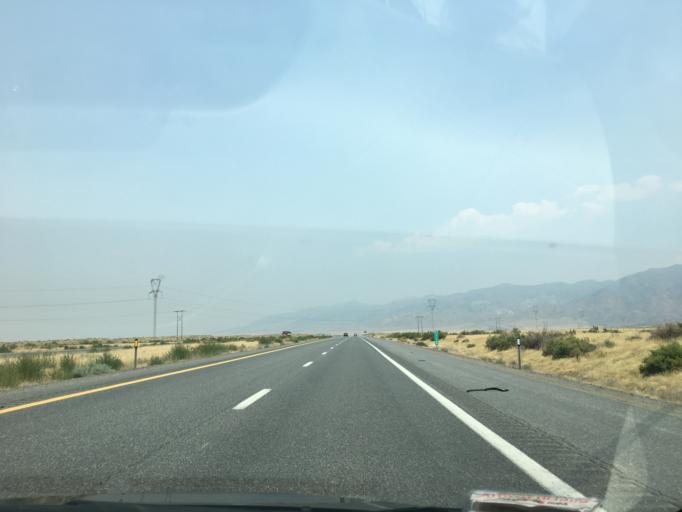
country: US
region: Nevada
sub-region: Pershing County
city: Lovelock
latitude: 40.3117
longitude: -118.3373
